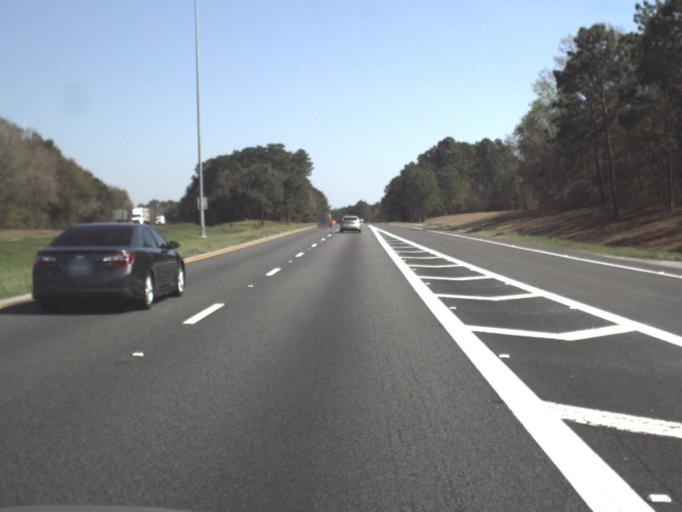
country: US
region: Florida
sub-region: Jackson County
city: Sneads
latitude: 30.6546
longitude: -85.0337
